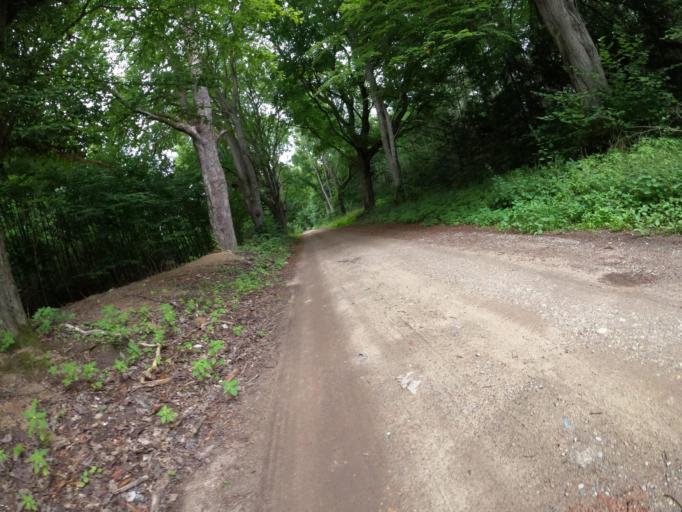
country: PL
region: West Pomeranian Voivodeship
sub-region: Powiat bialogardzki
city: Tychowo
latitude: 53.9847
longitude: 16.3848
